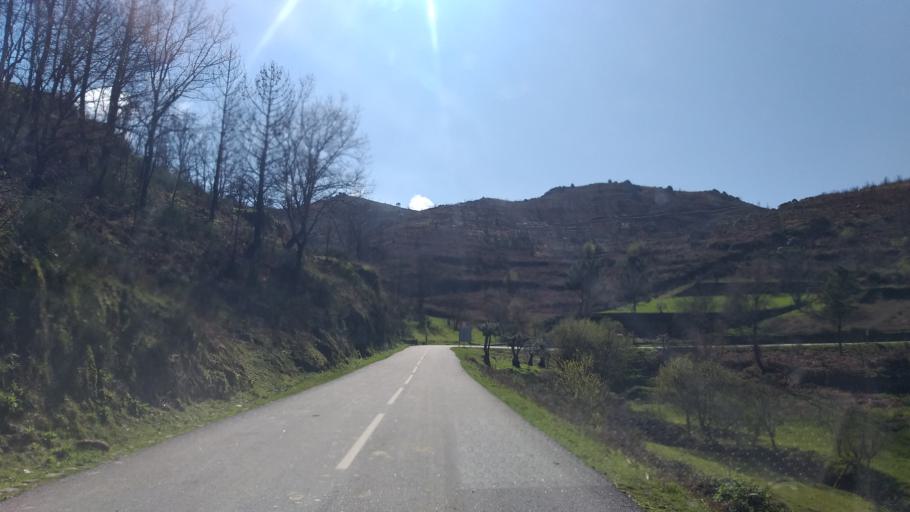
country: PT
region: Guarda
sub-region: Manteigas
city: Manteigas
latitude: 40.4631
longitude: -7.6092
